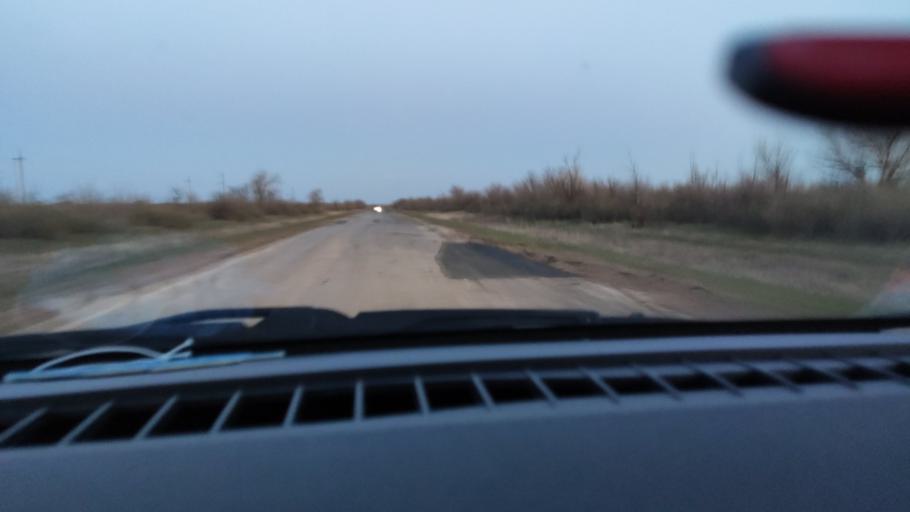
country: RU
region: Saratov
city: Rovnoye
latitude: 51.0514
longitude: 46.0413
